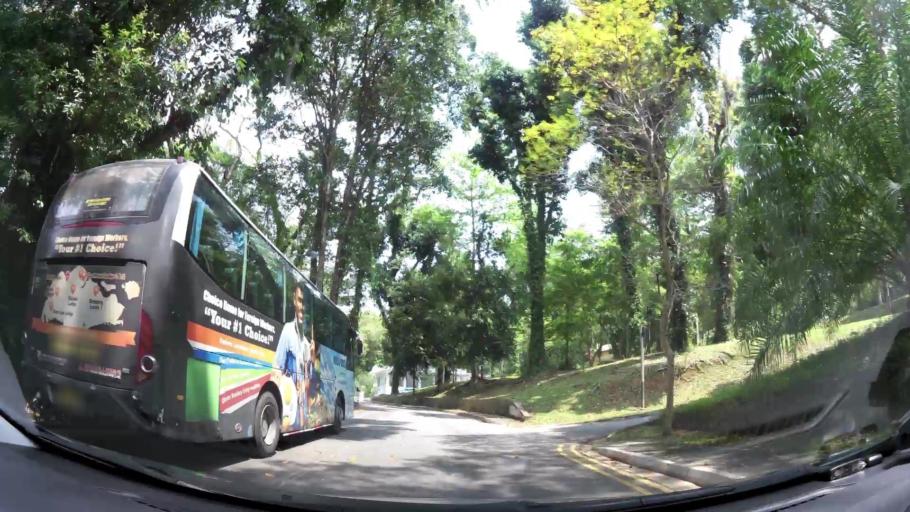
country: MY
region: Johor
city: Kampung Pasir Gudang Baru
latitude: 1.3900
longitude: 103.9788
